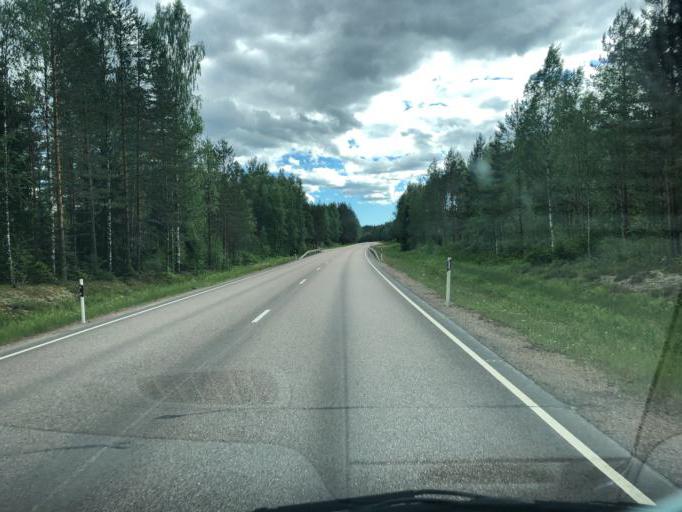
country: FI
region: Southern Savonia
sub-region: Mikkeli
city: Maentyharju
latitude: 61.1244
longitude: 27.1017
